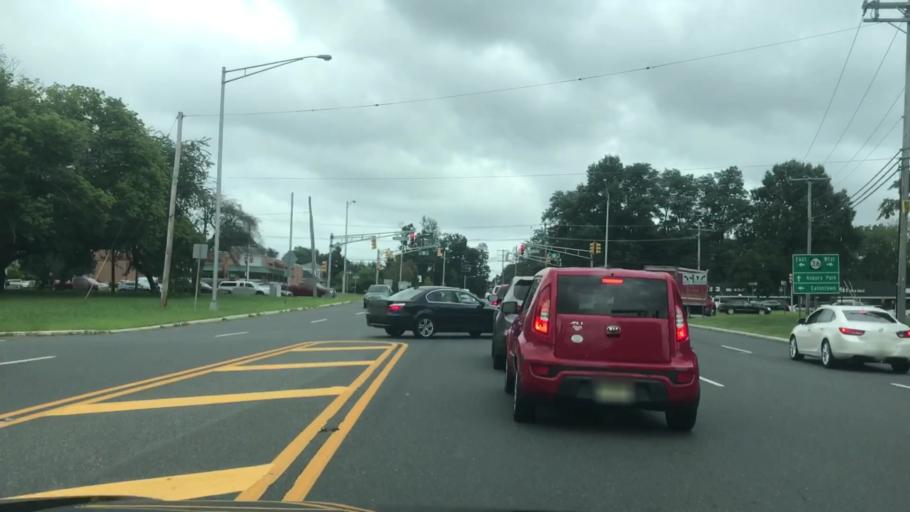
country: US
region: New Jersey
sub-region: Monmouth County
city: West Long Branch
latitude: 40.2961
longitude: -74.0297
